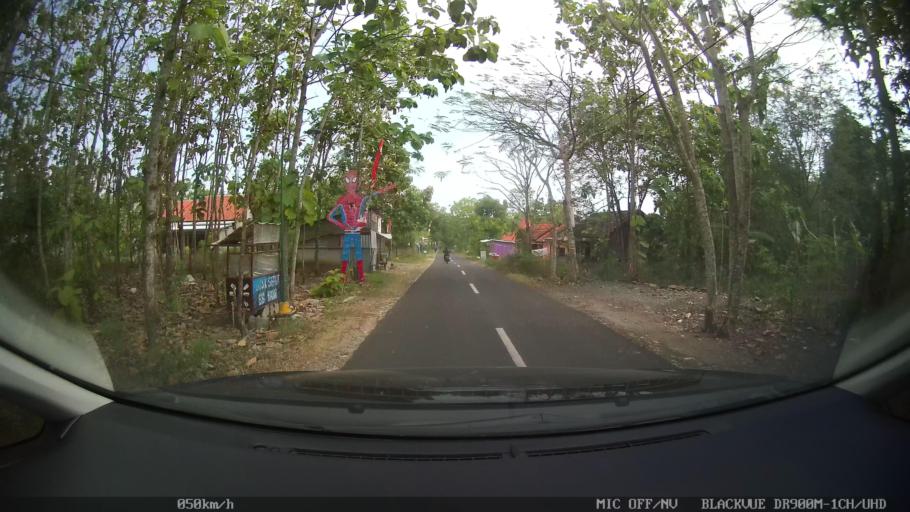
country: ID
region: Daerah Istimewa Yogyakarta
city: Kasihan
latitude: -7.8555
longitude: 110.3104
